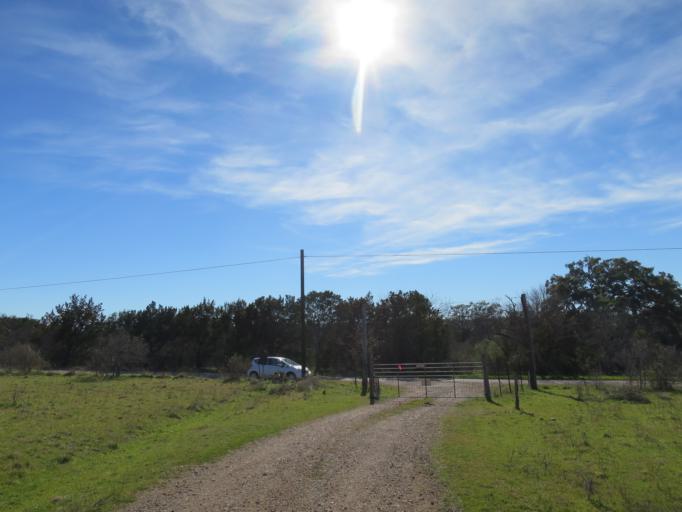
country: US
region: Texas
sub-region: Burnet County
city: Marble Falls
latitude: 30.5009
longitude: -98.1979
